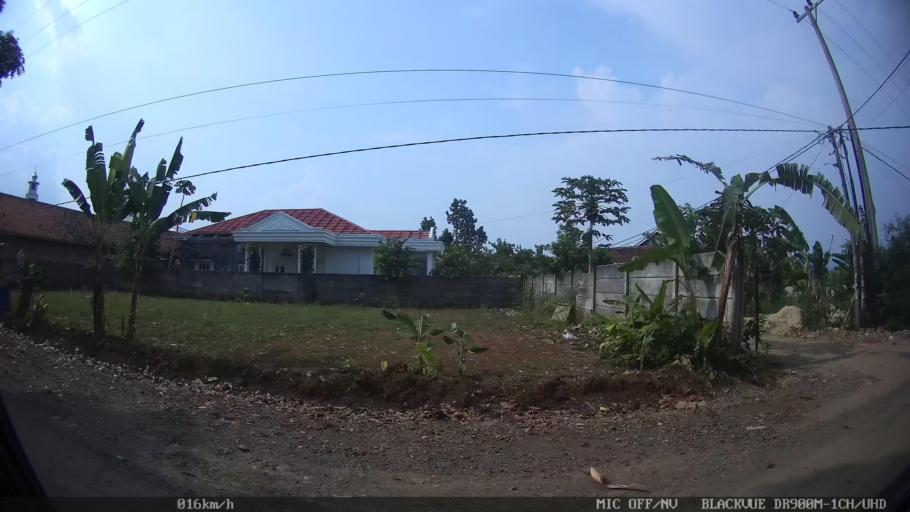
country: ID
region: Lampung
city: Kedaton
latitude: -5.3612
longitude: 105.2148
